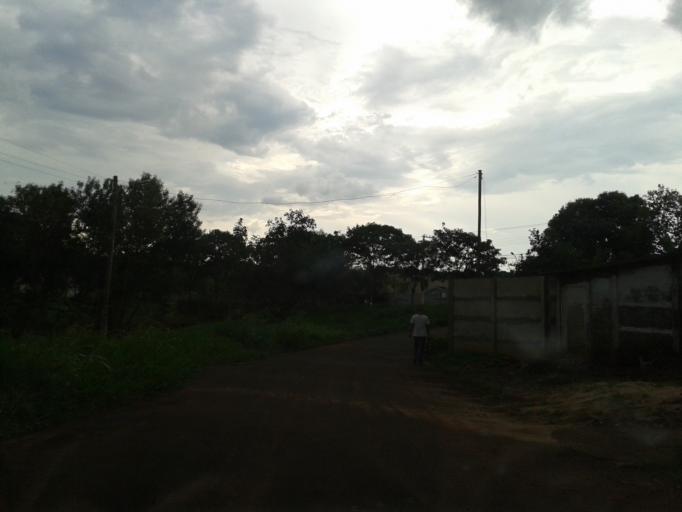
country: BR
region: Minas Gerais
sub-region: Ituiutaba
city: Ituiutaba
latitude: -18.9667
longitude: -49.4704
